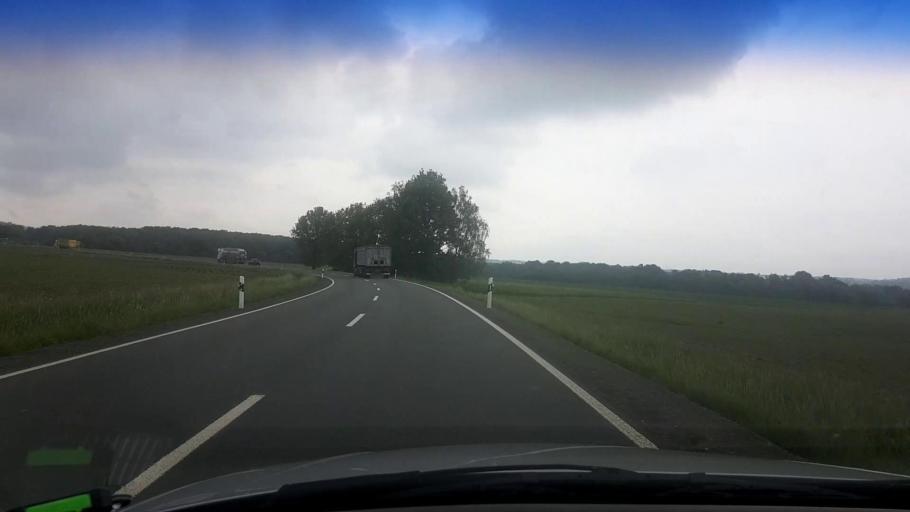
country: DE
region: Bavaria
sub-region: Upper Franconia
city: Gesees
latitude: 50.0193
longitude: 11.6640
